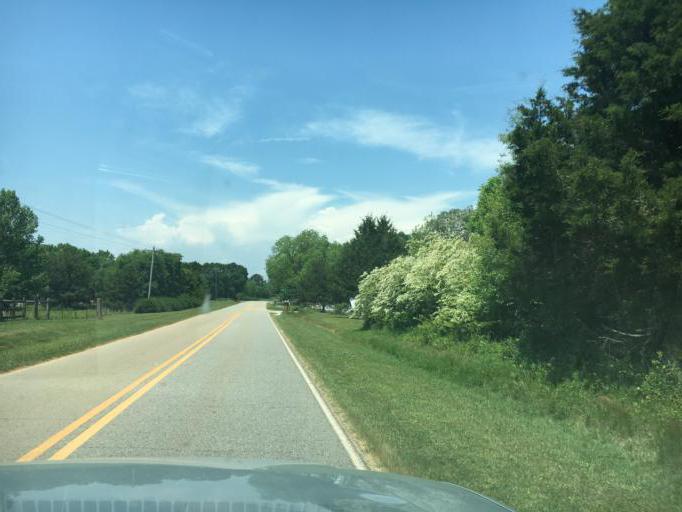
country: US
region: Georgia
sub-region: Hart County
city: Royston
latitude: 34.3005
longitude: -83.0911
